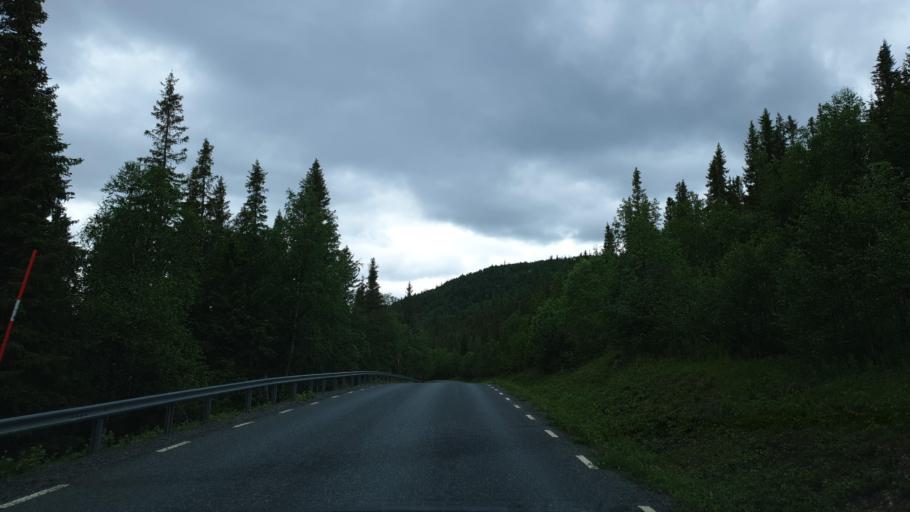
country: SE
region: Vaesterbotten
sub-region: Vilhelmina Kommun
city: Sjoberg
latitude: 65.2563
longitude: 15.4054
